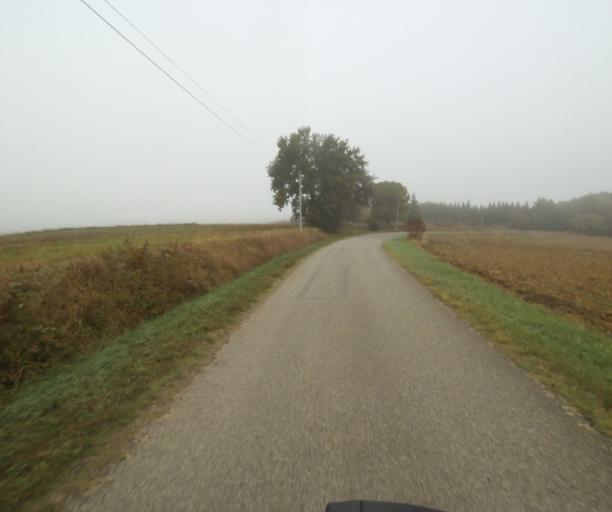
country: FR
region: Midi-Pyrenees
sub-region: Departement du Tarn-et-Garonne
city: Nohic
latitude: 43.9301
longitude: 1.4648
